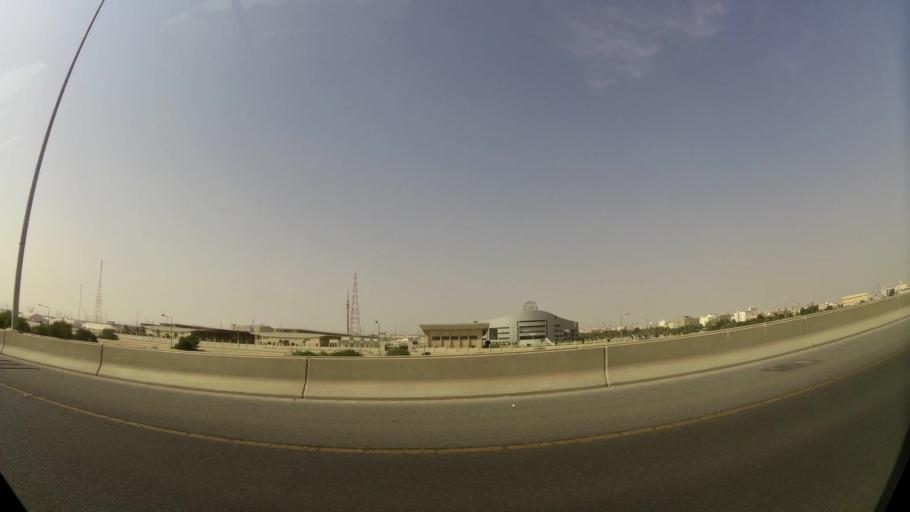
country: KW
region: Al Ahmadi
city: Al Fahahil
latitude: 29.0889
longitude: 48.1155
